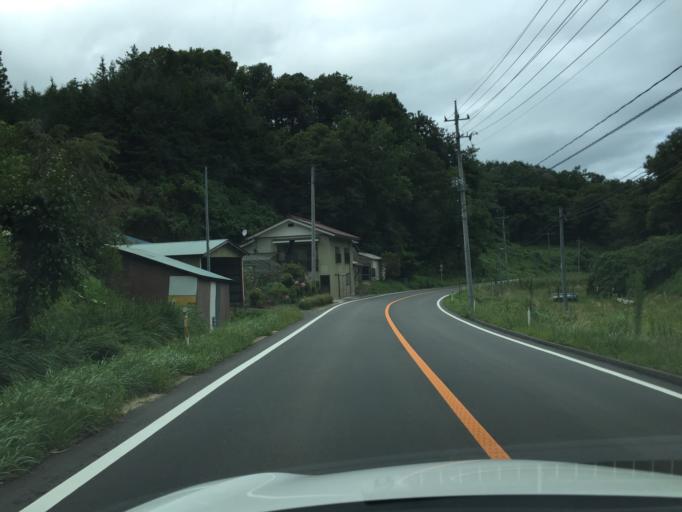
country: JP
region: Fukushima
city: Funehikimachi-funehiki
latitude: 37.4662
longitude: 140.5706
